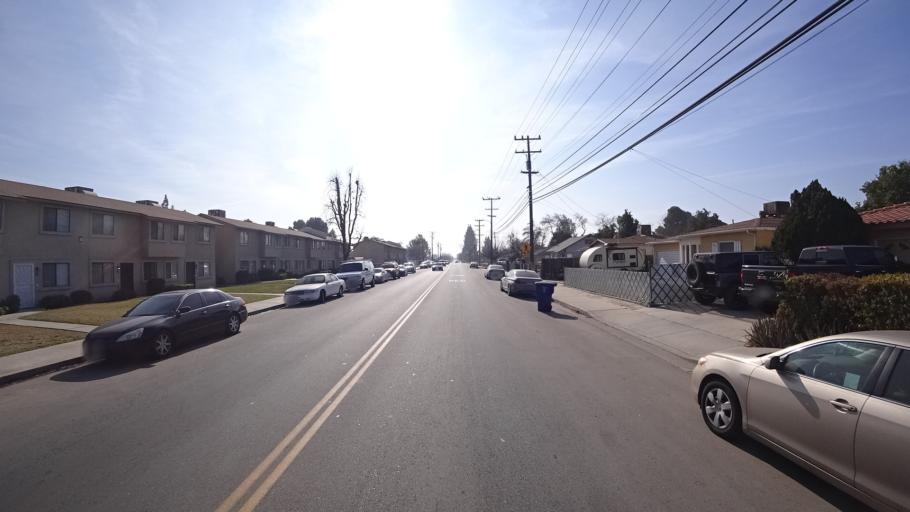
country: US
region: California
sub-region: Kern County
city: Bakersfield
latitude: 35.3638
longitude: -119.0434
